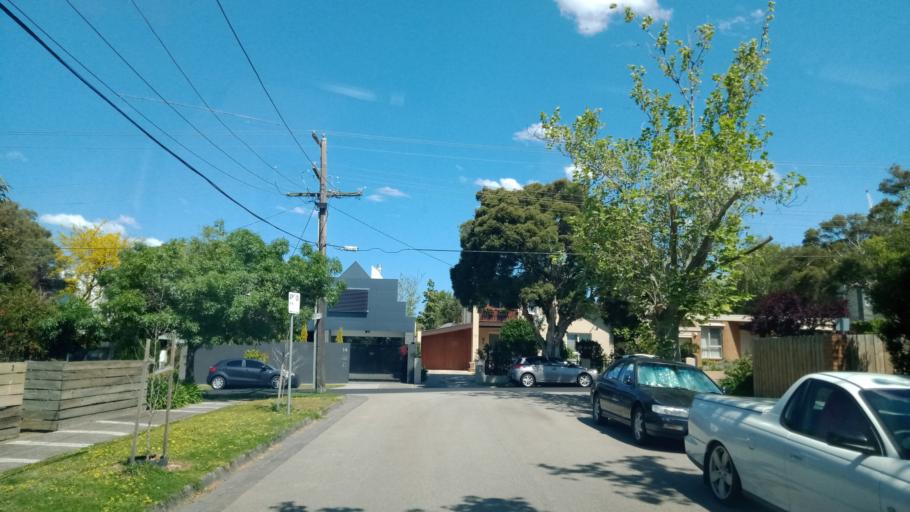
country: AU
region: Victoria
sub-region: Stonnington
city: Glen Iris
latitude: -37.8497
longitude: 145.0381
